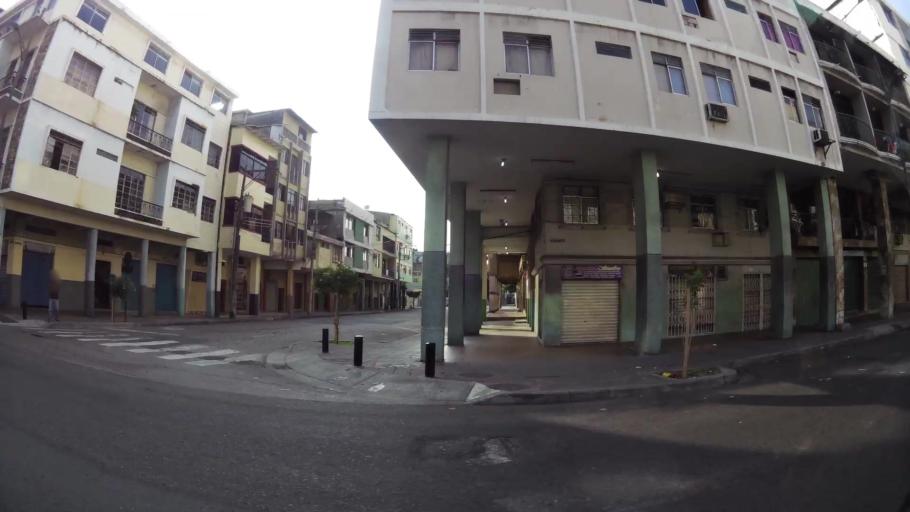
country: EC
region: Guayas
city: Guayaquil
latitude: -2.1979
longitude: -79.8879
